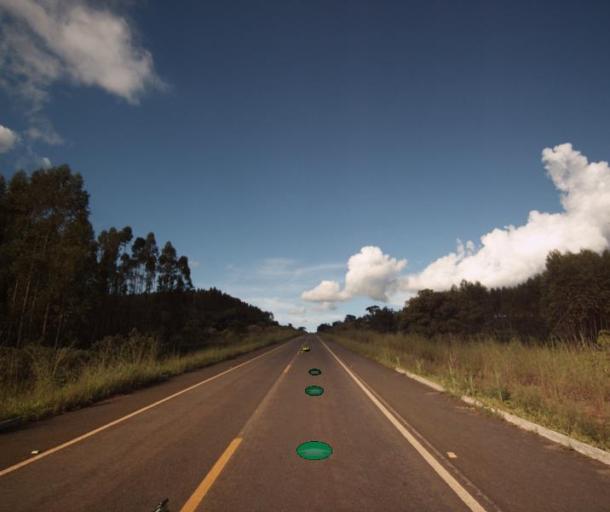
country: BR
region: Goias
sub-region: Itaberai
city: Itaberai
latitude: -15.9875
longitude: -49.7134
